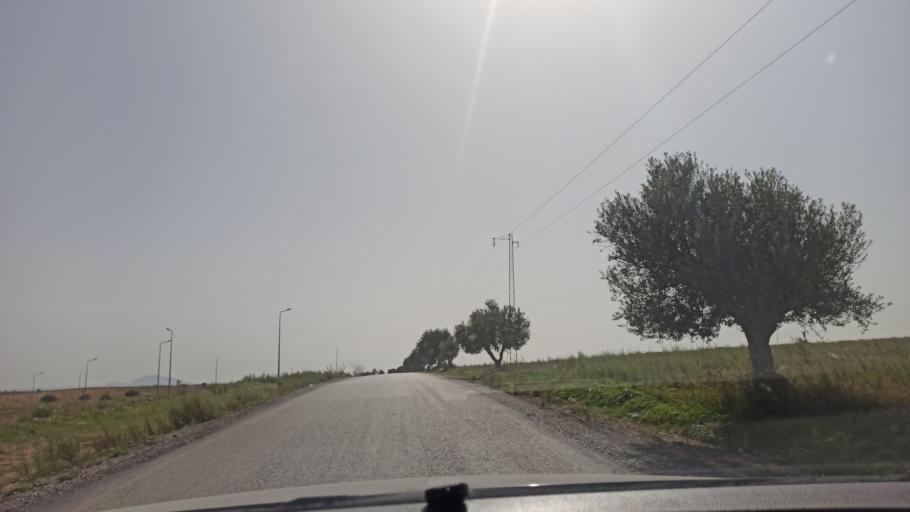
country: TN
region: Manouba
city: Manouba
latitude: 36.7366
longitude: 10.0840
